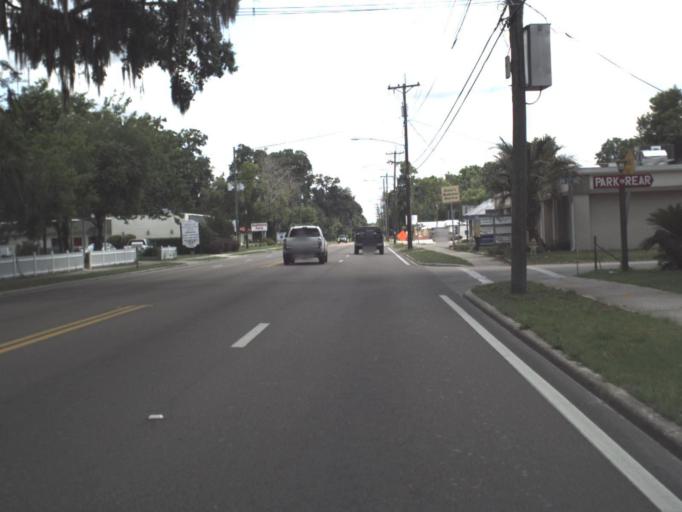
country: US
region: Florida
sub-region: Alachua County
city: Gainesville
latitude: 29.6769
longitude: -82.3307
